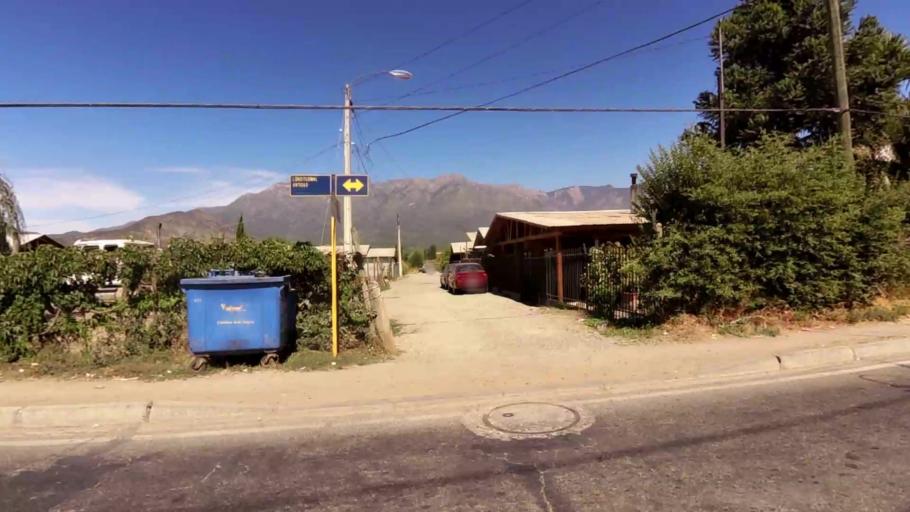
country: CL
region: O'Higgins
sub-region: Provincia de Cachapoal
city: Graneros
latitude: -33.9661
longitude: -70.7130
